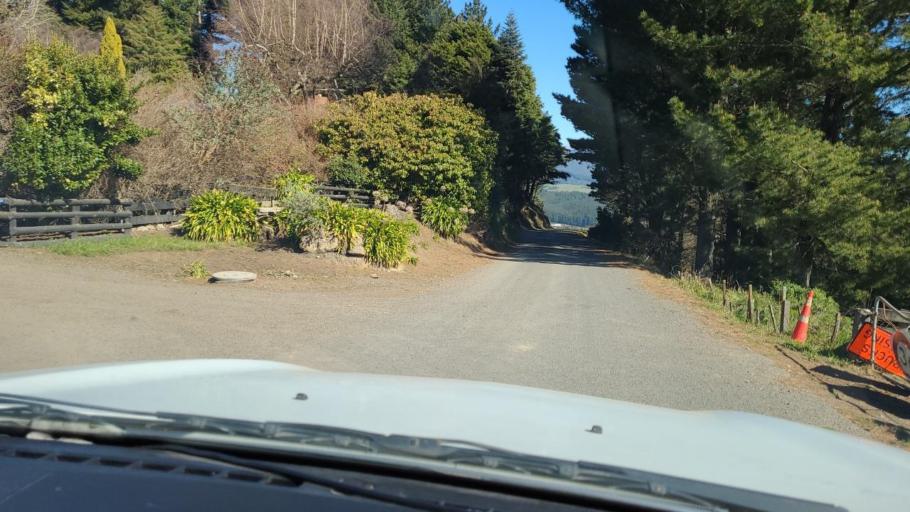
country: NZ
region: Hawke's Bay
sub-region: Napier City
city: Taradale
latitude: -39.4708
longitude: 176.4014
